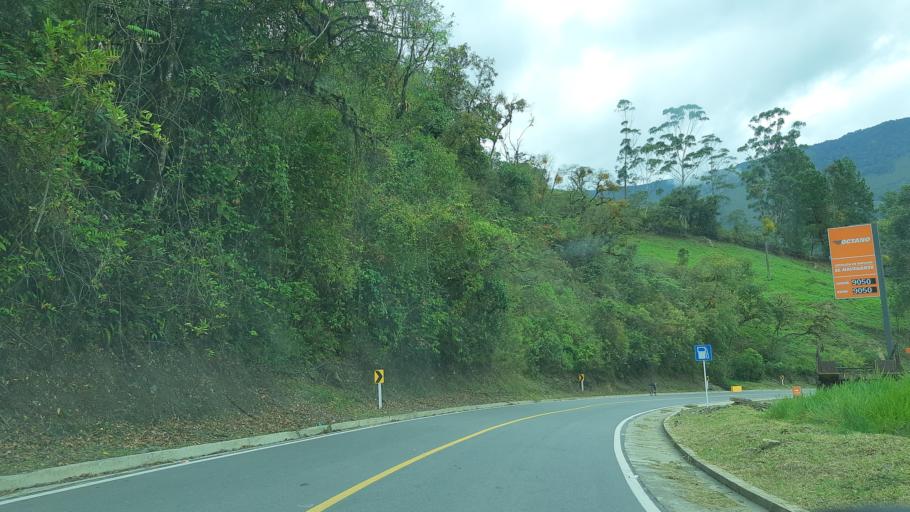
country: CO
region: Boyaca
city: Chivor
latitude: 4.9567
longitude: -73.3113
